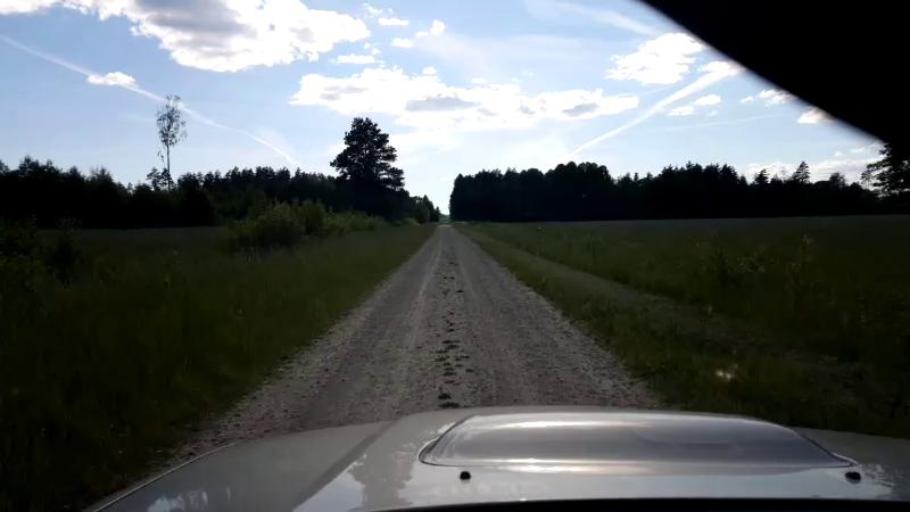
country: EE
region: Paernumaa
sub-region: Sindi linn
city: Sindi
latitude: 58.4946
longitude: 24.6175
